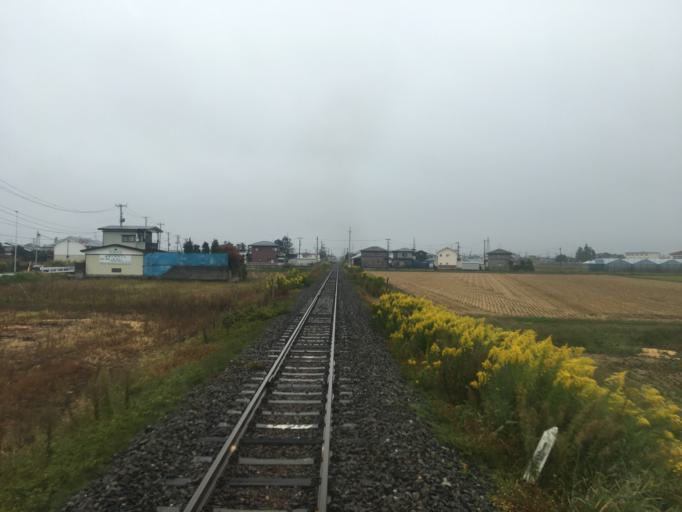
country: JP
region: Miyagi
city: Furukawa
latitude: 38.5728
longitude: 140.9323
